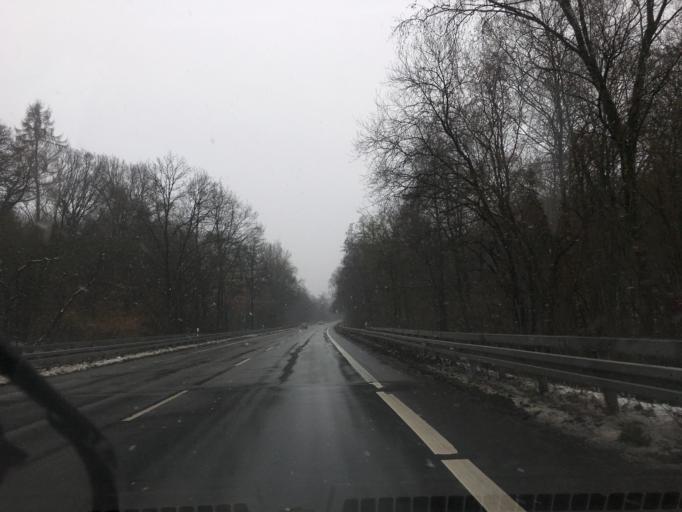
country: DE
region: North Rhine-Westphalia
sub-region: Regierungsbezirk Munster
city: Klein Reken
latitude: 51.7977
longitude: 7.0325
